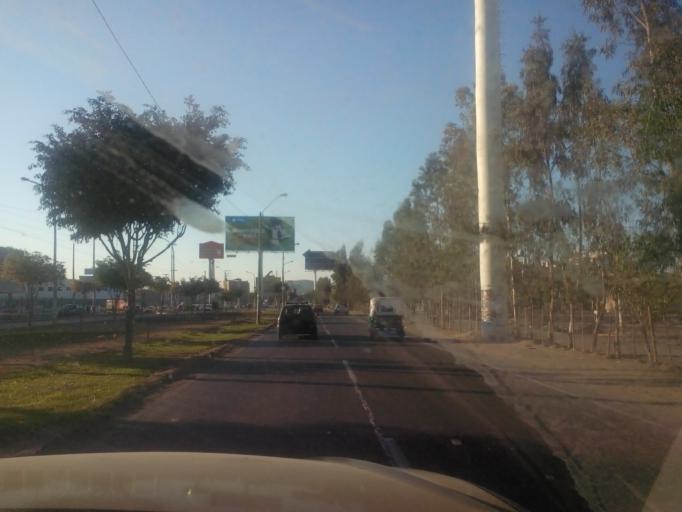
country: PE
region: Ica
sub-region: Provincia de Ica
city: Ica
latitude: -14.0758
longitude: -75.7384
